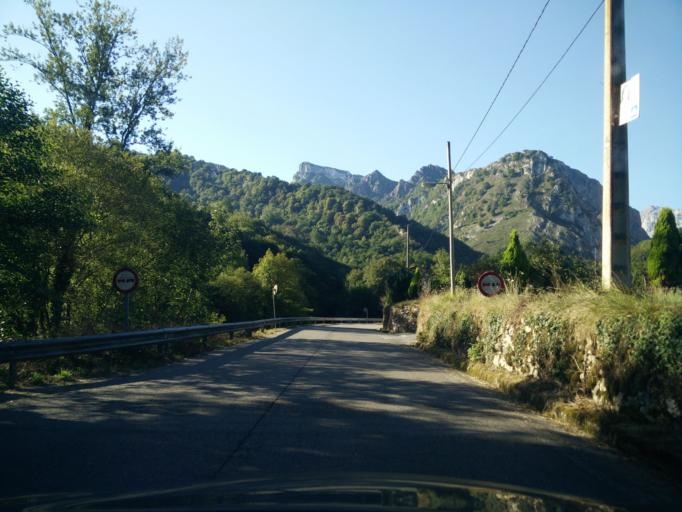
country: ES
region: Asturias
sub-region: Province of Asturias
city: Parres
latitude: 43.2553
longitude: -5.1995
